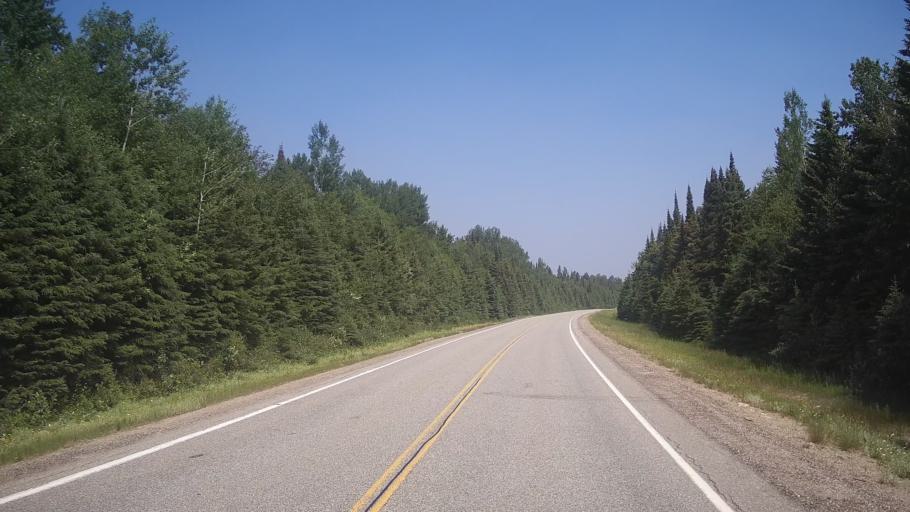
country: CA
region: Ontario
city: Timmins
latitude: 48.0822
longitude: -81.5966
